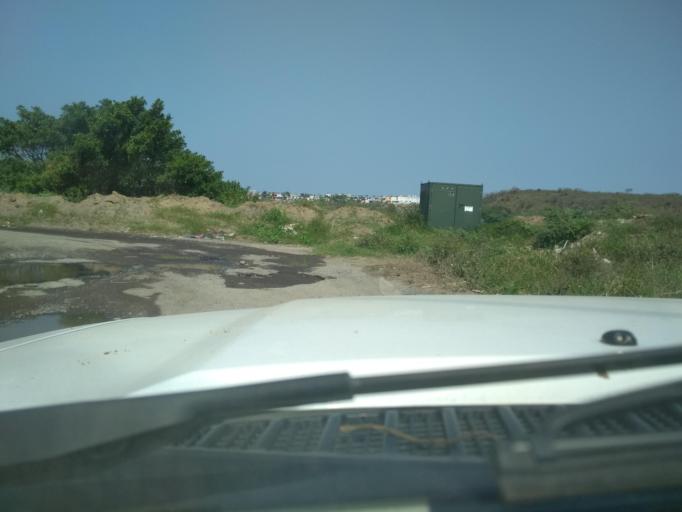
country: MX
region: Veracruz
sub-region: Veracruz
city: Lomas de Rio Medio Cuatro
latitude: 19.1937
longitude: -96.2078
